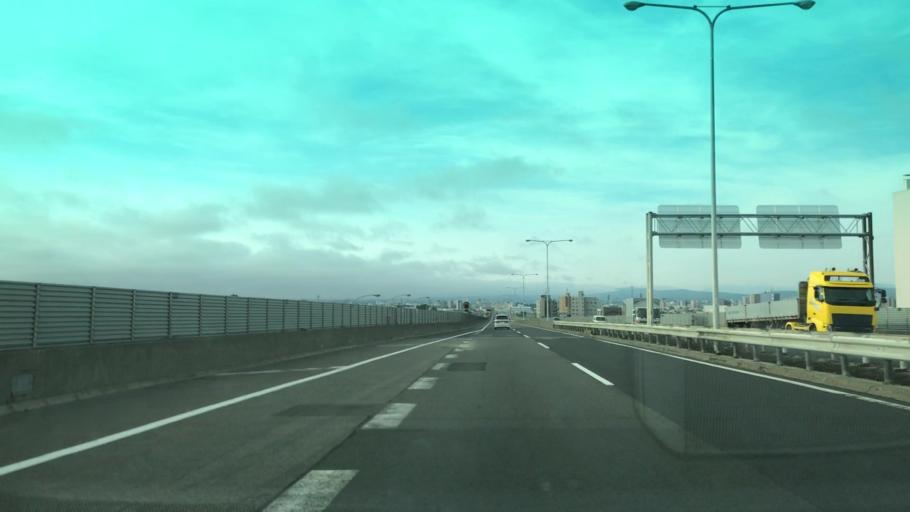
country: JP
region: Hokkaido
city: Sapporo
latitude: 43.0731
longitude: 141.4216
